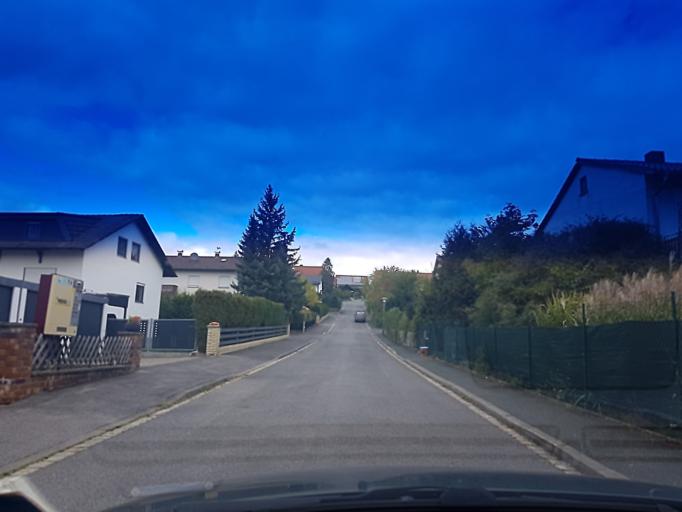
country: DE
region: Bavaria
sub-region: Upper Franconia
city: Strullendorf
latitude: 49.8550
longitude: 10.9967
